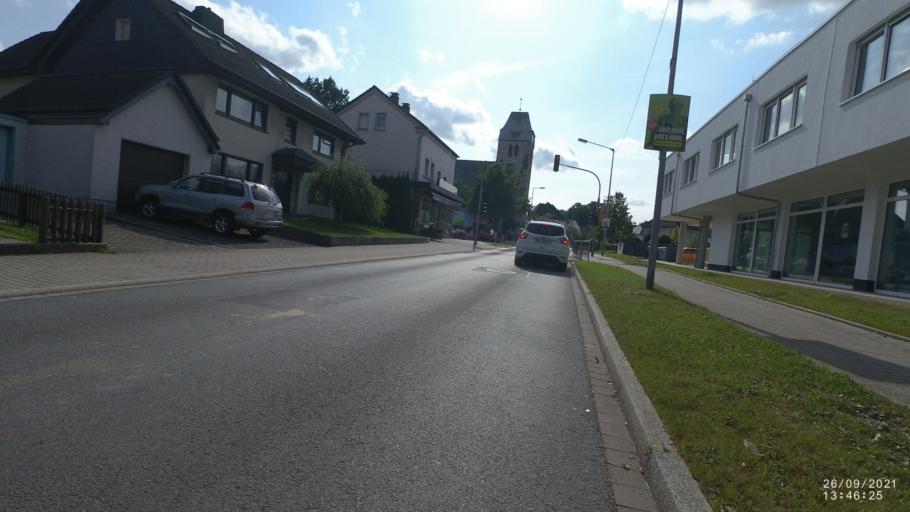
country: DE
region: North Rhine-Westphalia
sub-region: Regierungsbezirk Arnsberg
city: Frondenberg
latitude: 51.4574
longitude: 7.7587
